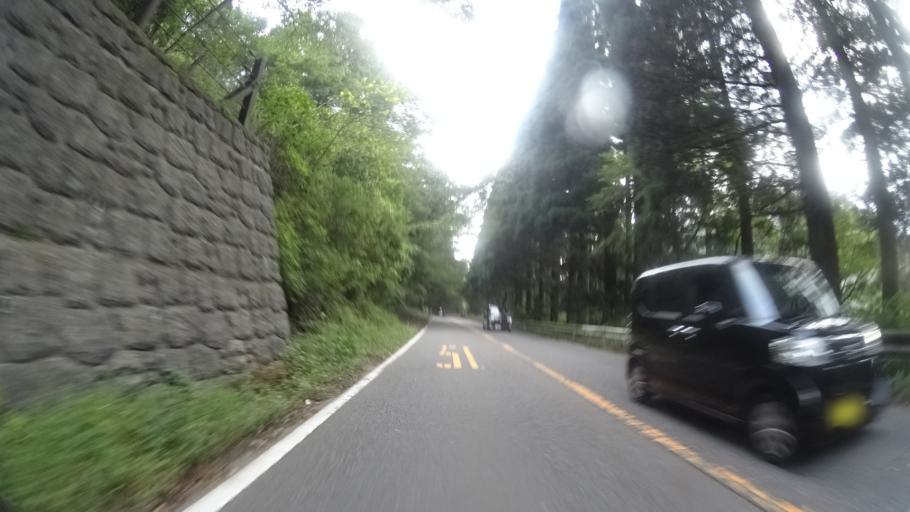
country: JP
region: Oita
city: Beppu
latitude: 33.2725
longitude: 131.4164
